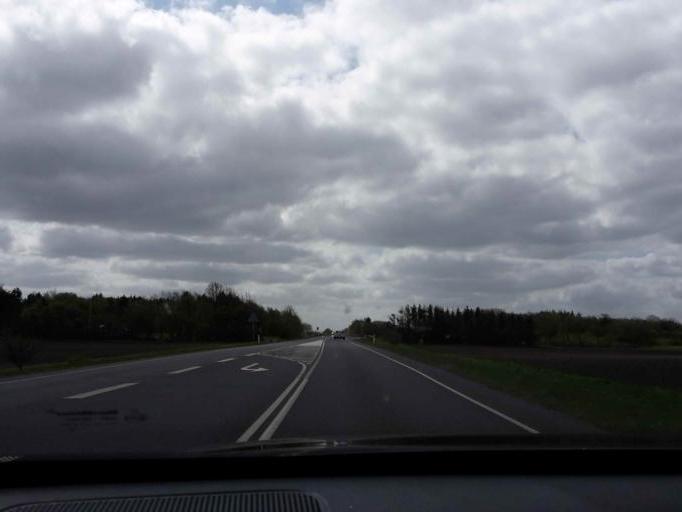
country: DK
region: South Denmark
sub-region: Varde Kommune
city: Olgod
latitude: 55.7763
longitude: 8.6236
